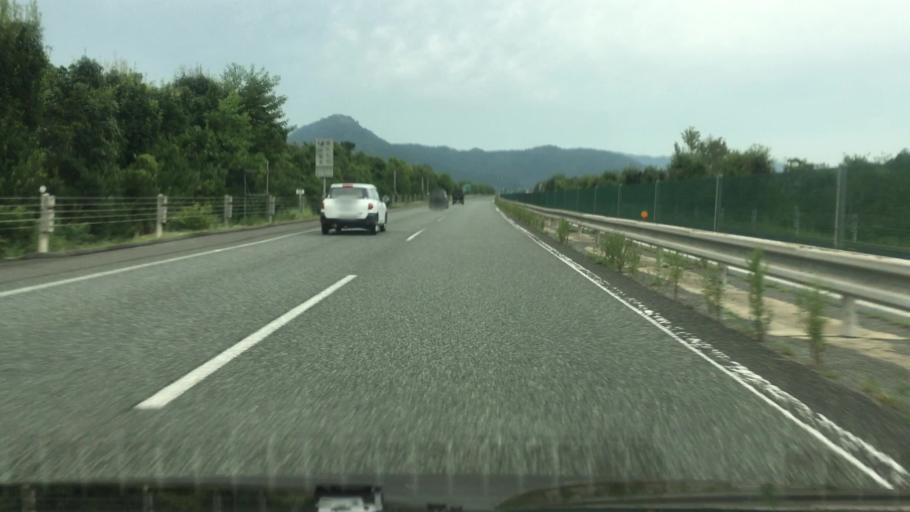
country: JP
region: Hyogo
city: Sasayama
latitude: 35.1515
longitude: 135.1229
